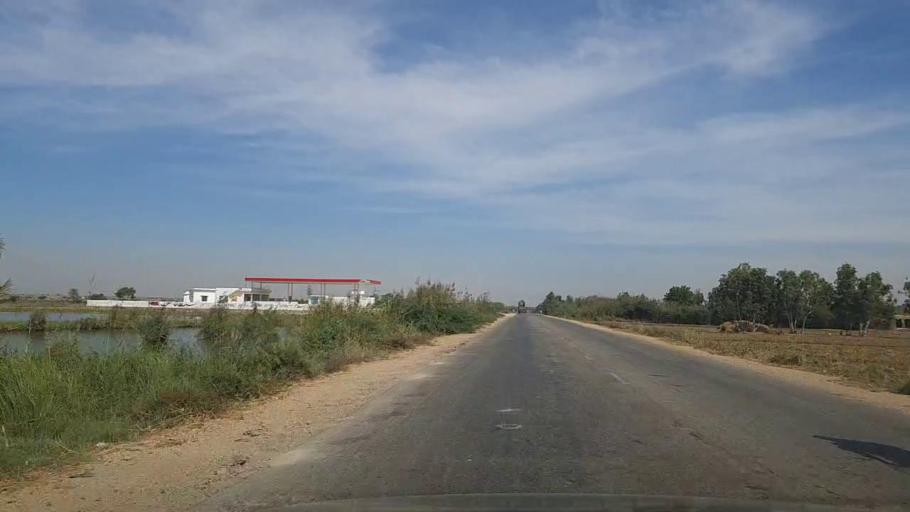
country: PK
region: Sindh
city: Daro Mehar
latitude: 24.9777
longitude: 68.1290
